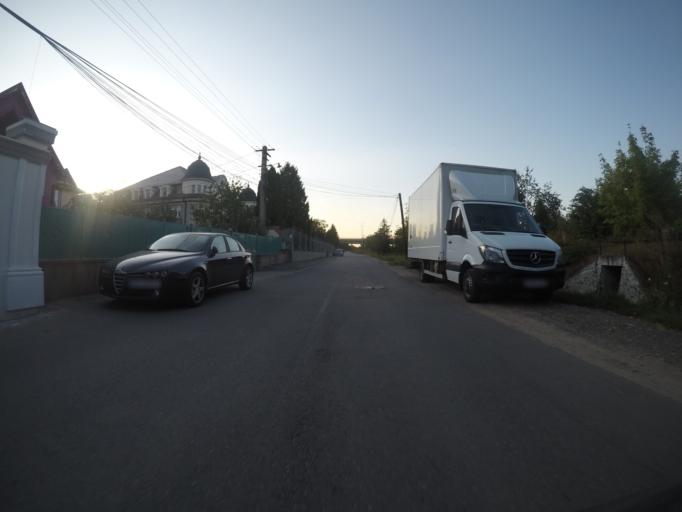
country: RO
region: Sibiu
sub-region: Comuna Selimbar
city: Selimbar
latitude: 45.7874
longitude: 24.1786
